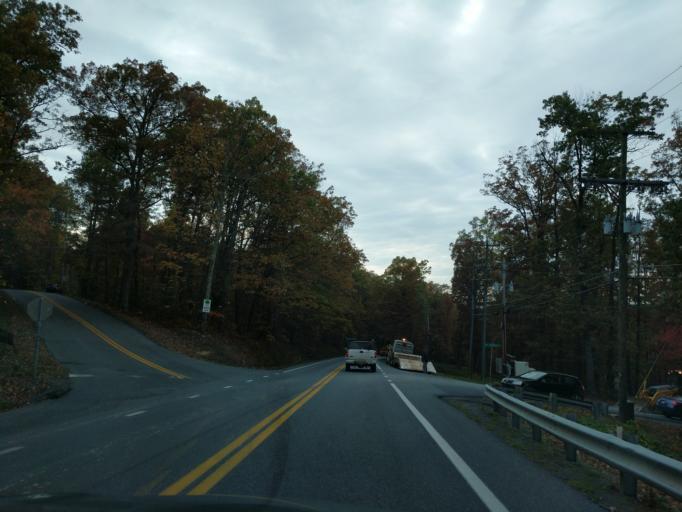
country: US
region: West Virginia
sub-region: Berkeley County
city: Inwood
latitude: 39.3859
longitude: -78.1195
